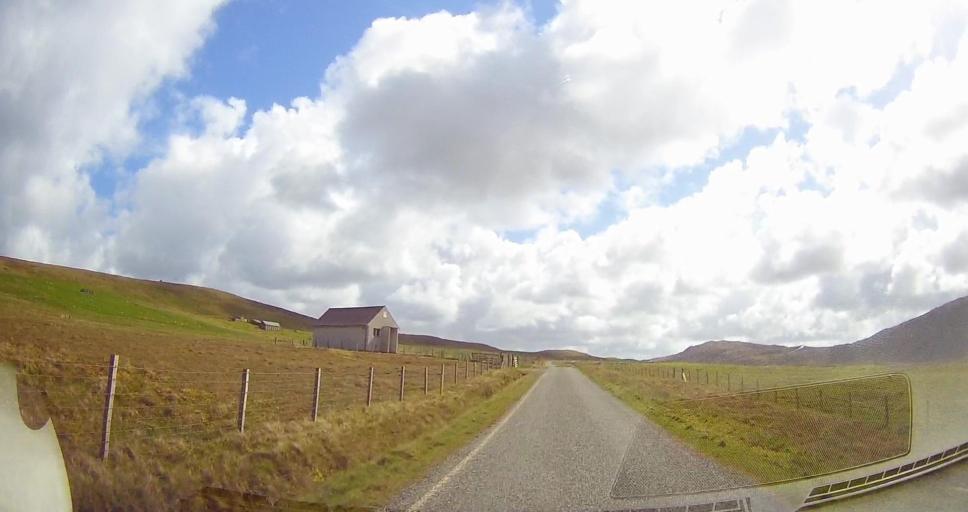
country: GB
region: Scotland
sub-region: Shetland Islands
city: Lerwick
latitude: 60.5709
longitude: -1.3325
